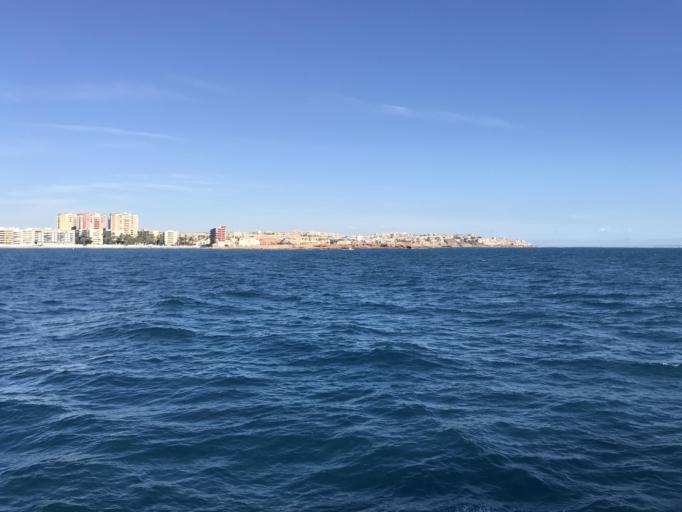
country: ES
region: Valencia
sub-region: Provincia de Alicante
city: Torrevieja
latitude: 37.9775
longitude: -0.6550
